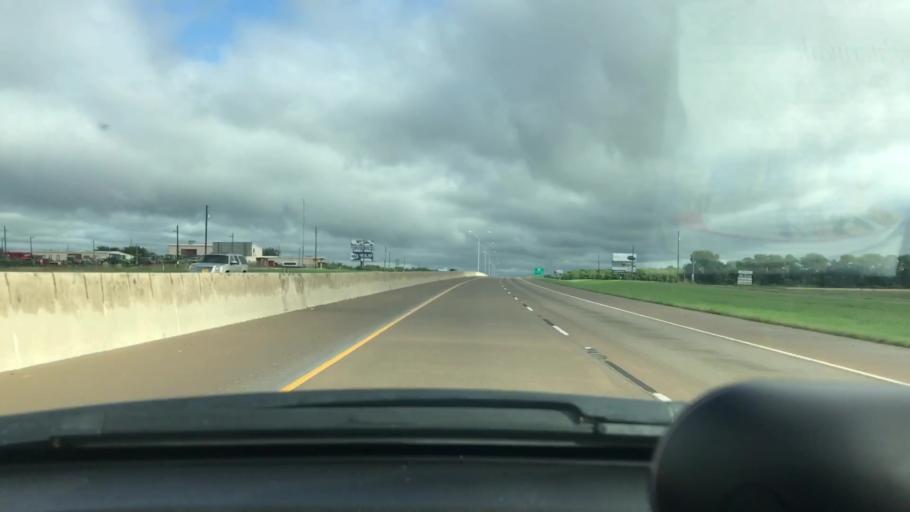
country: US
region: Texas
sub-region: Grayson County
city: Howe
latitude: 33.4841
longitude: -96.6201
